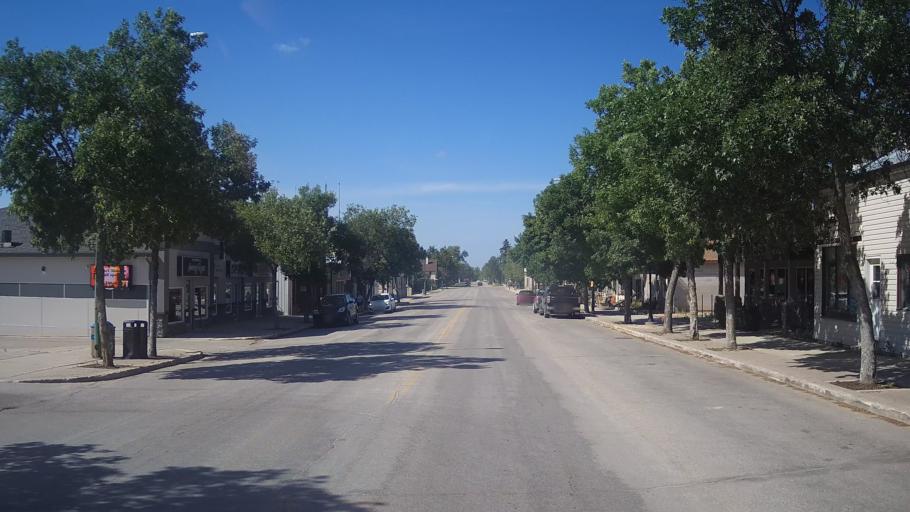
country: CA
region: Manitoba
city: Stonewall
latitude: 50.1352
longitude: -97.3266
